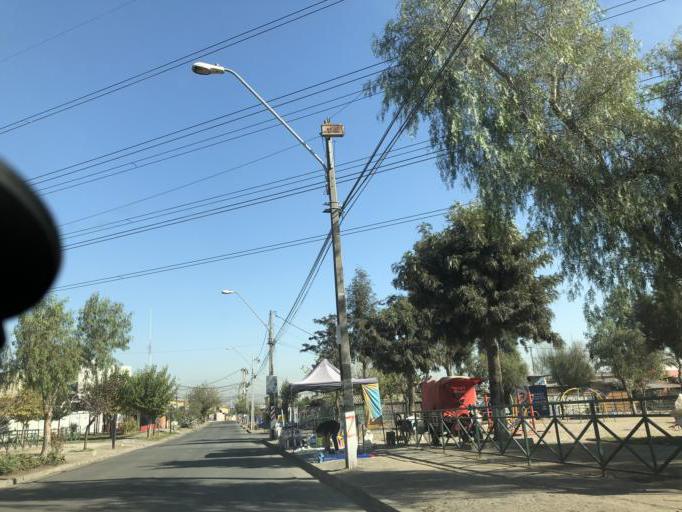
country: CL
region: Santiago Metropolitan
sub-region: Provincia de Santiago
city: La Pintana
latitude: -33.6196
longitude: -70.6181
